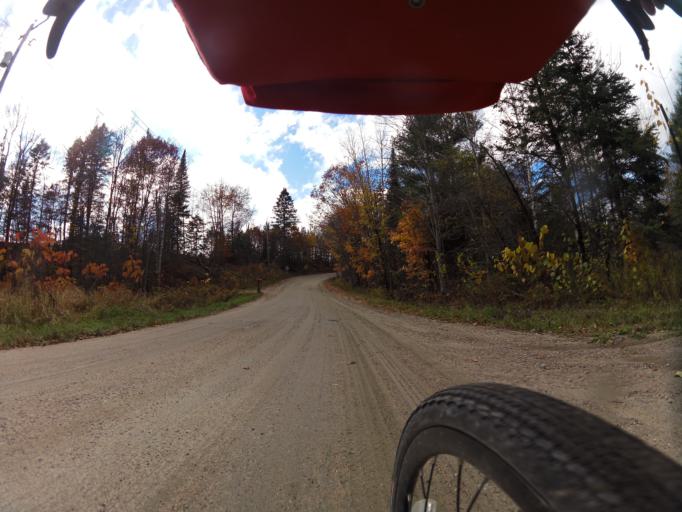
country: CA
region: Quebec
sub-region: Outaouais
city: Wakefield
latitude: 45.6971
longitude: -76.0540
